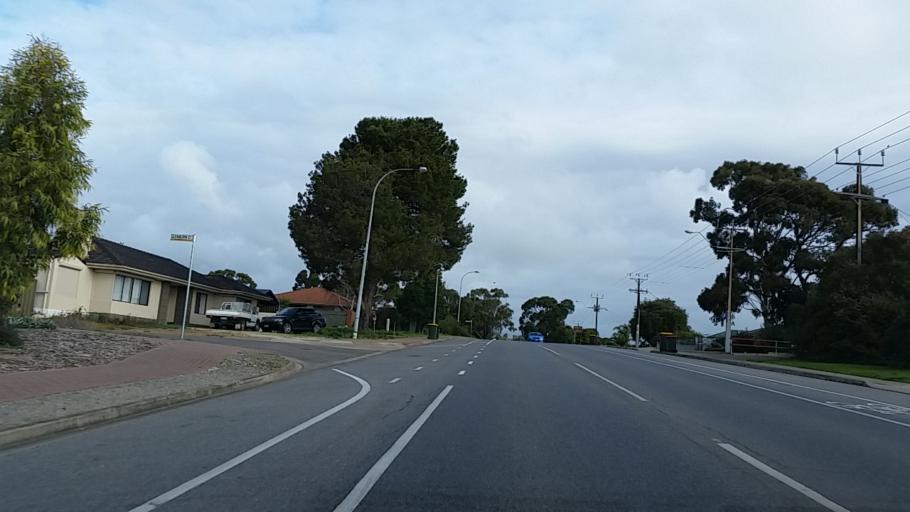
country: AU
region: South Australia
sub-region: Onkaparinga
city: Morphett Vale
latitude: -35.1406
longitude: 138.5375
